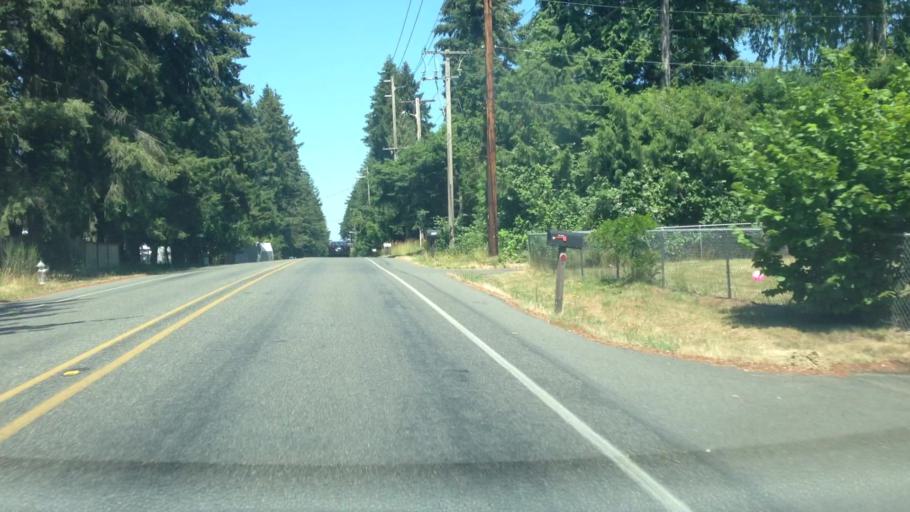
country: US
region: Washington
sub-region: Pierce County
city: South Hill
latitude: 47.1436
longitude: -122.3148
